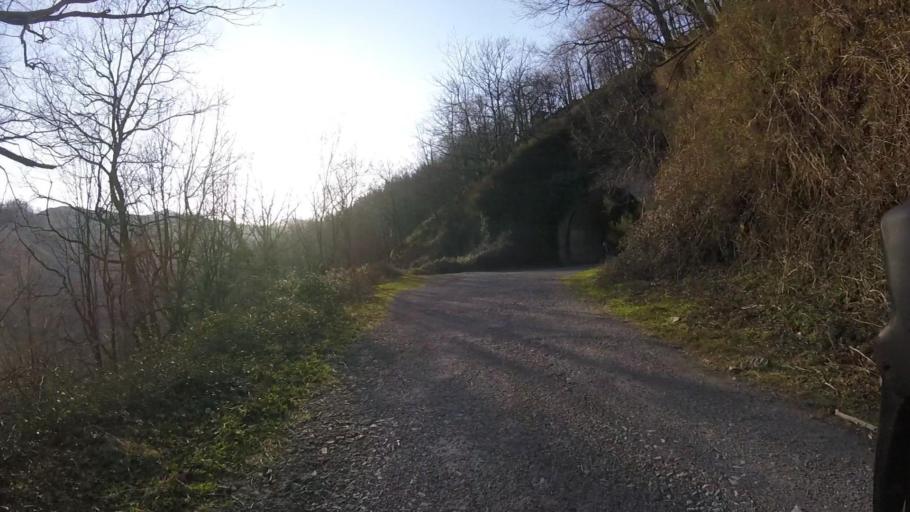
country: ES
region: Navarre
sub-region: Provincia de Navarra
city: Arano
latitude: 43.2113
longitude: -1.8603
